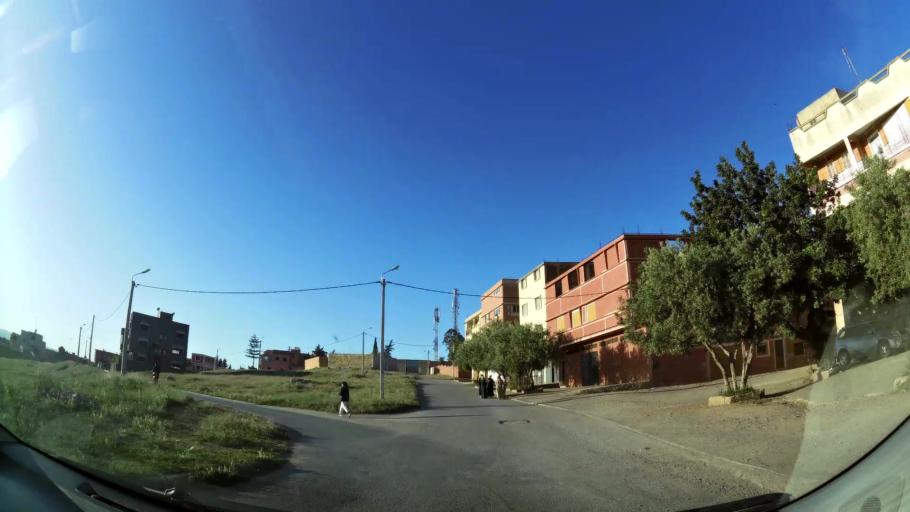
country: MA
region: Oriental
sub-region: Berkane-Taourirt
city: Berkane
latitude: 34.9258
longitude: -2.3223
